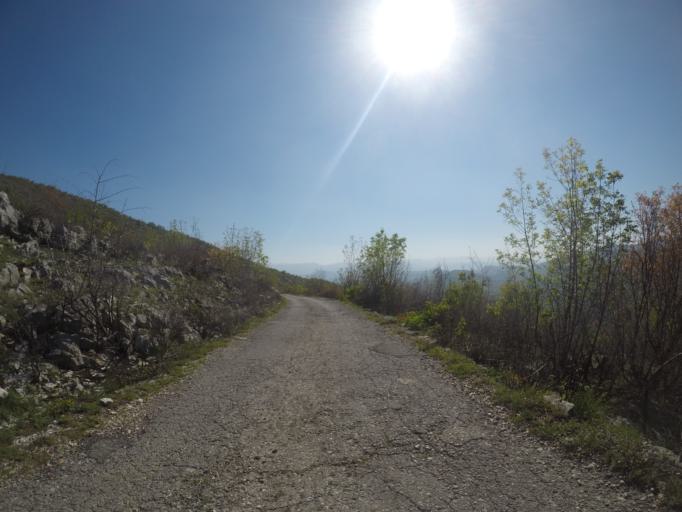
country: ME
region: Danilovgrad
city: Danilovgrad
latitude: 42.5146
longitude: 19.0732
